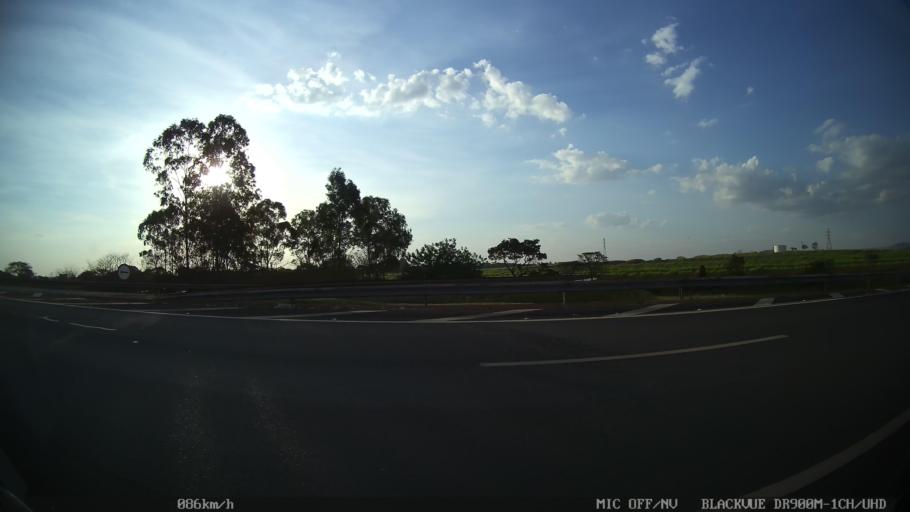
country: BR
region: Sao Paulo
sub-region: Ribeirao Preto
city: Ribeirao Preto
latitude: -21.1122
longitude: -47.7793
